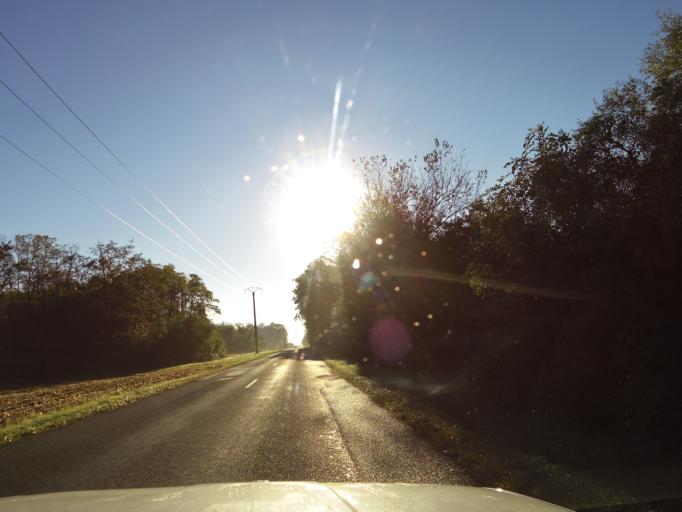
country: FR
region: Rhone-Alpes
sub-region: Departement de l'Ain
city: Leyment
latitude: 45.8829
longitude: 5.2995
